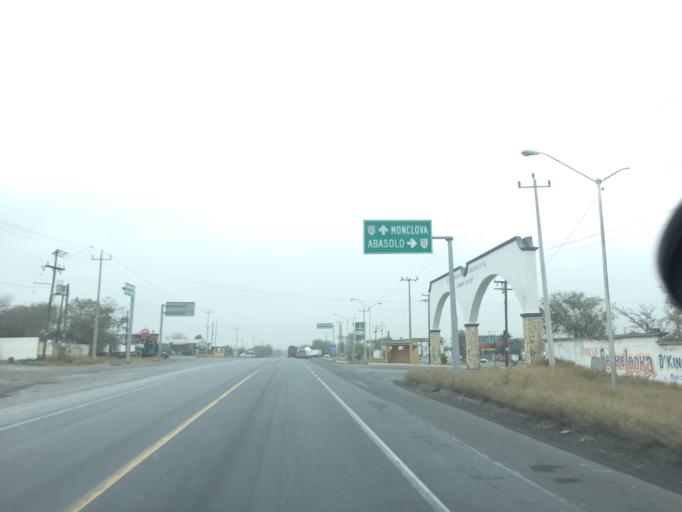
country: MX
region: Nuevo Leon
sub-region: Salinas Victoria
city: Las Torres
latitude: 25.9394
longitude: -100.4036
